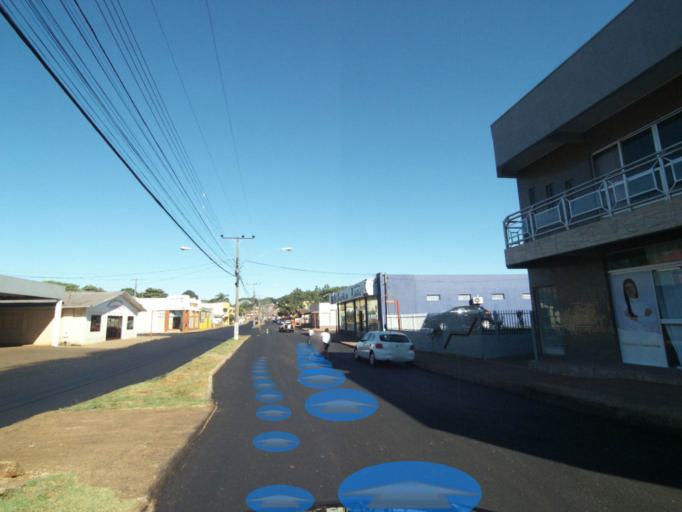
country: BR
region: Parana
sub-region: Coronel Vivida
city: Coronel Vivida
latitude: -26.1425
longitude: -52.3857
